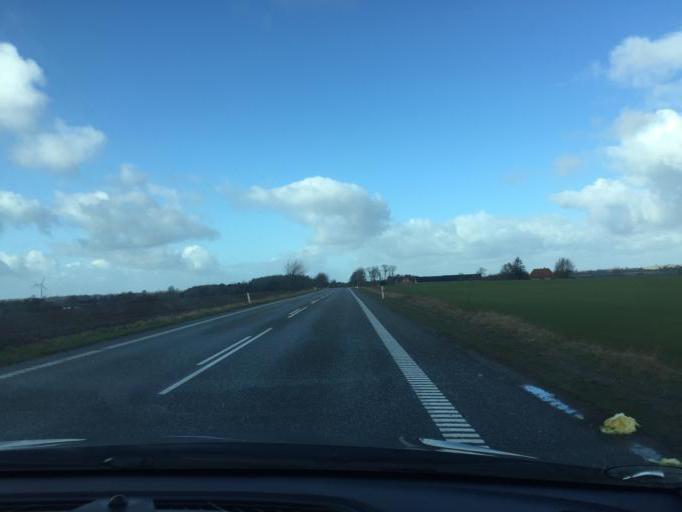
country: DK
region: South Denmark
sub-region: Middelfart Kommune
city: Ejby
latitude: 55.4605
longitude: 9.9342
